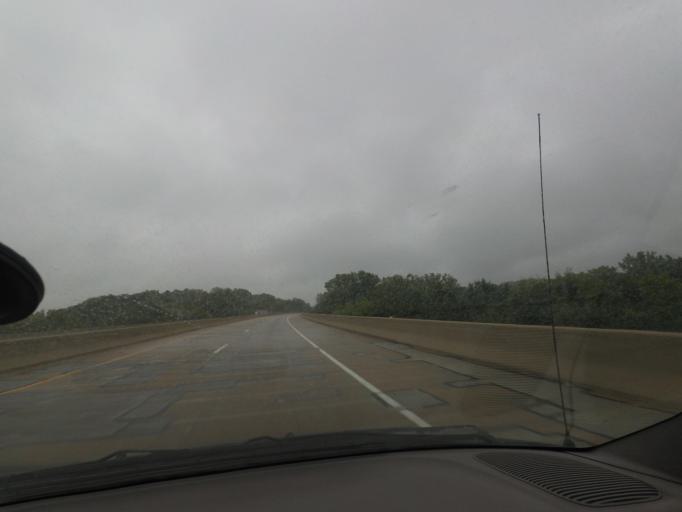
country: US
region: Illinois
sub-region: Pike County
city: Barry
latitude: 39.7158
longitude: -91.0664
